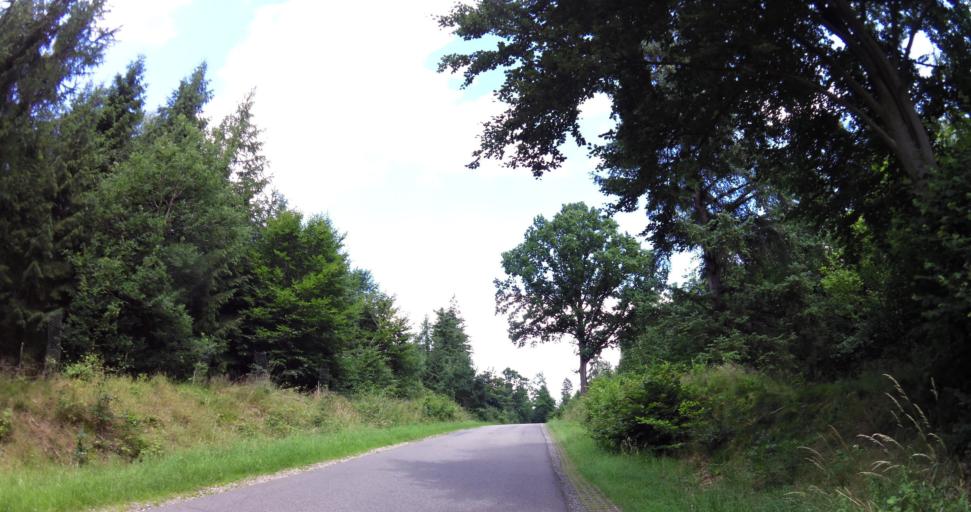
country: DE
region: Schleswig-Holstein
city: Brodersby
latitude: 54.5108
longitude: 9.7197
